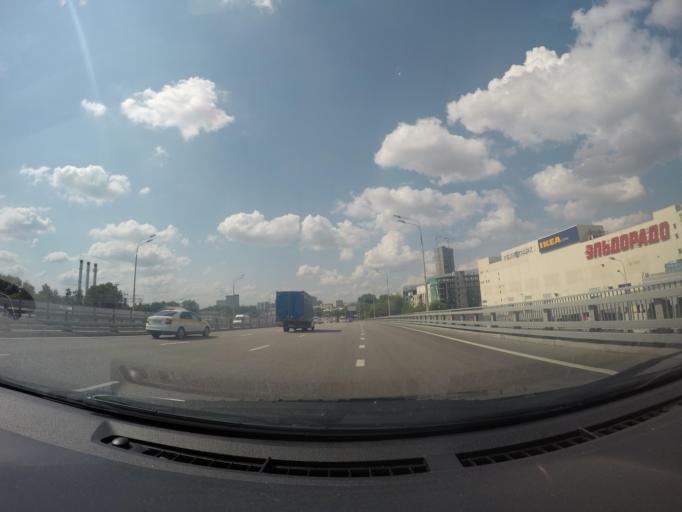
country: RU
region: Moscow
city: Leonovo
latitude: 55.8433
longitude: 37.6590
